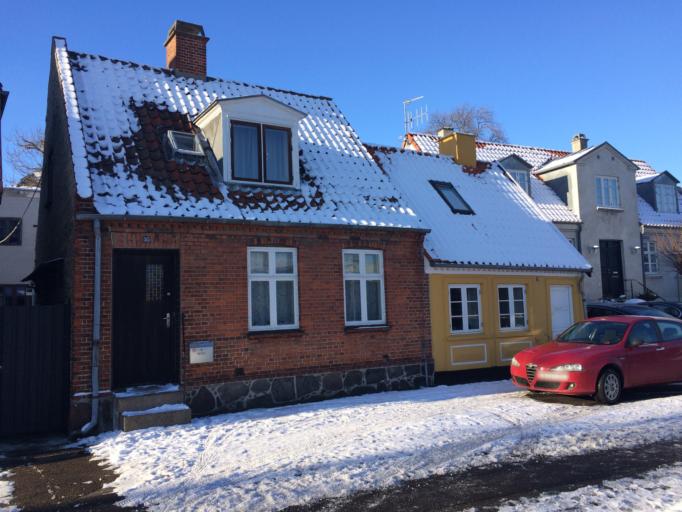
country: DK
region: Zealand
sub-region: Roskilde Kommune
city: Roskilde
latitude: 55.6489
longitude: 12.0773
